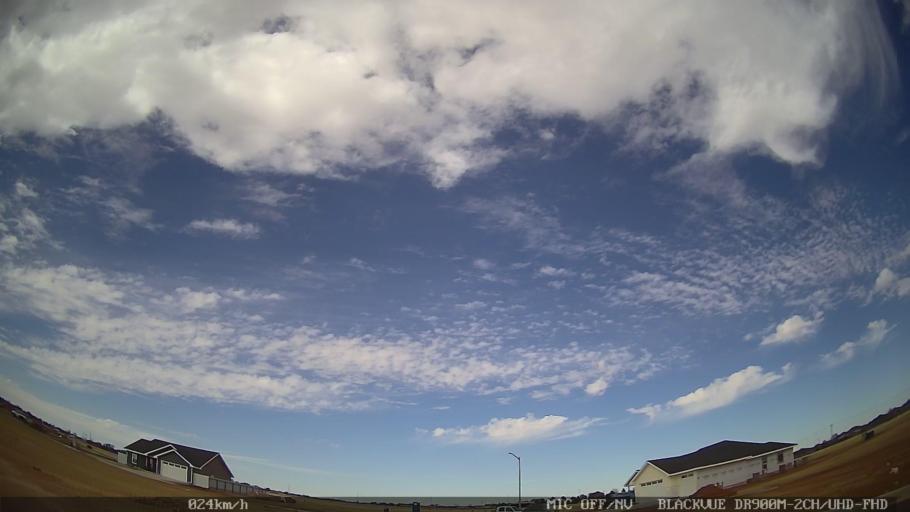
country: US
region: New Mexico
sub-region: Curry County
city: Clovis
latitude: 34.4205
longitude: -103.1629
